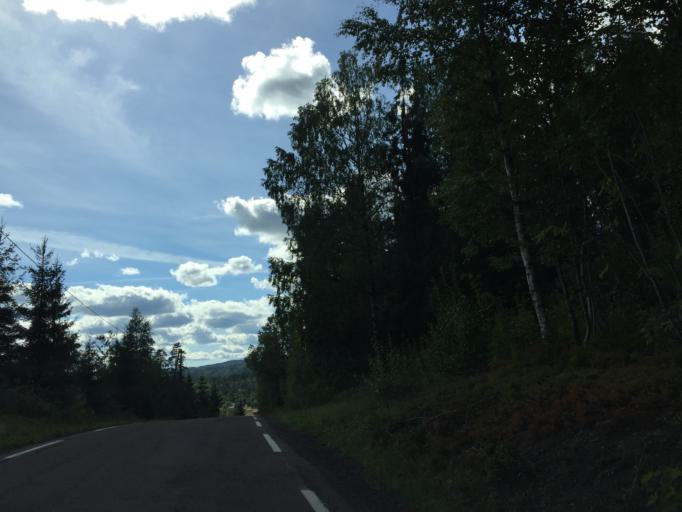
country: NO
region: Vestfold
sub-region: Hof
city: Hof
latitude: 59.4326
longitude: 10.1420
